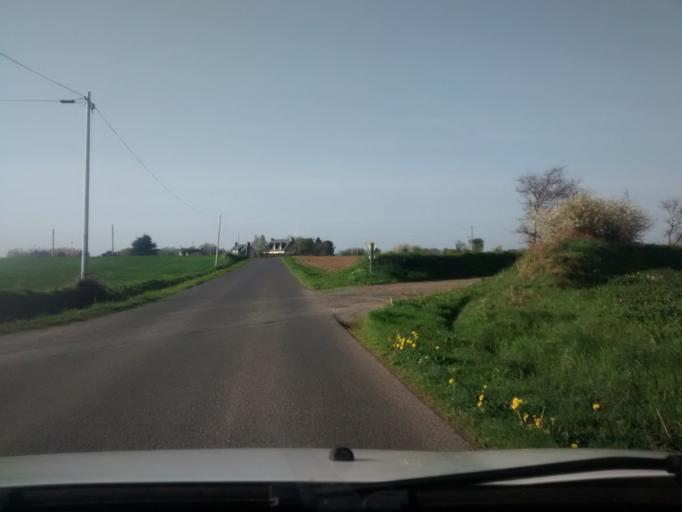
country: FR
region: Brittany
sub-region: Departement des Cotes-d'Armor
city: Trevou-Treguignec
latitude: 48.8058
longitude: -3.3520
